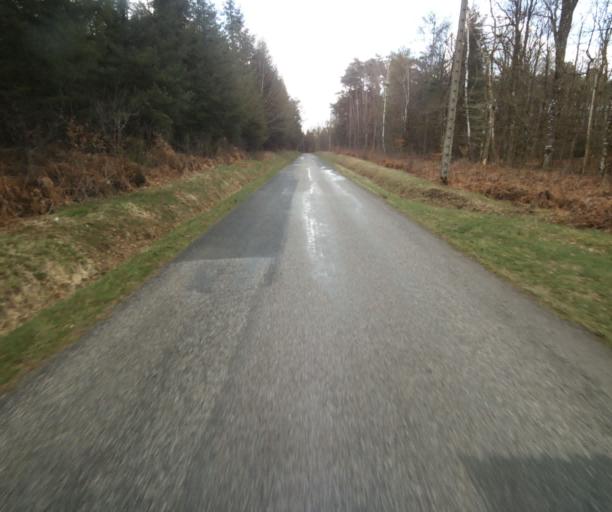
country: FR
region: Limousin
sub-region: Departement de la Correze
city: Correze
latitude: 45.2503
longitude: 1.9290
